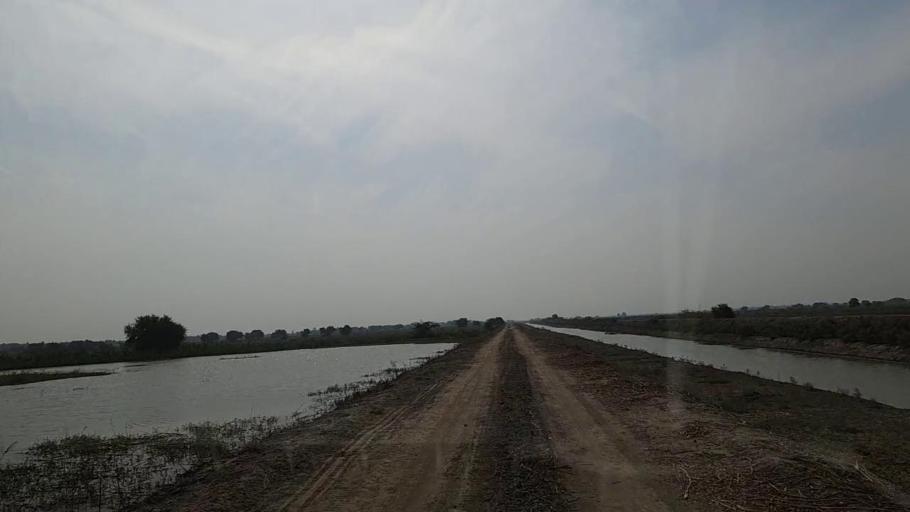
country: PK
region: Sindh
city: Mirpur Batoro
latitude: 24.6718
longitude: 68.2497
